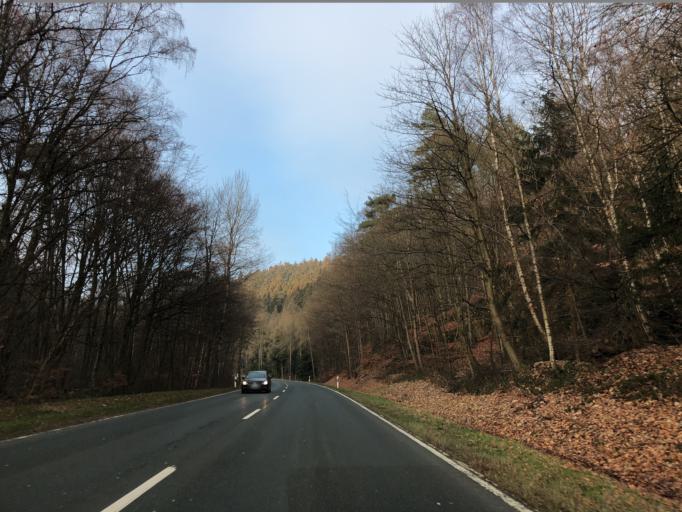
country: DE
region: Hesse
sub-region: Regierungsbezirk Darmstadt
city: Kronberg
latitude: 50.2236
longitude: 8.5193
